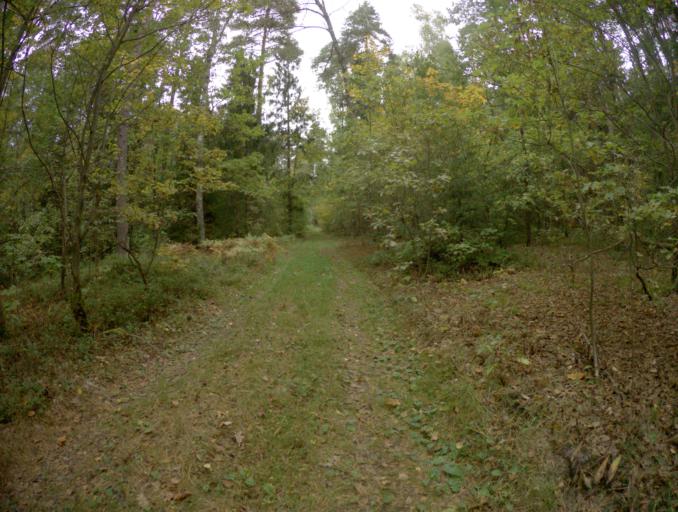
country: RU
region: Vladimir
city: Bogolyubovo
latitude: 56.1462
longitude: 40.5564
